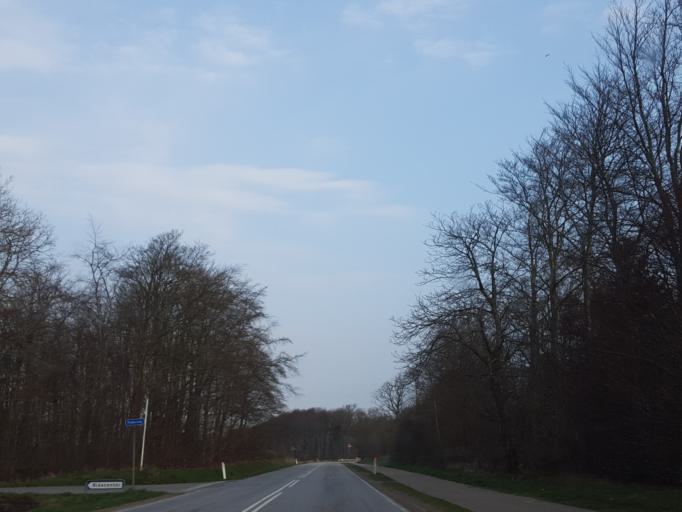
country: DK
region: South Denmark
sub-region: Esbjerg Kommune
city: Bramming
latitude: 55.4938
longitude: 8.6988
